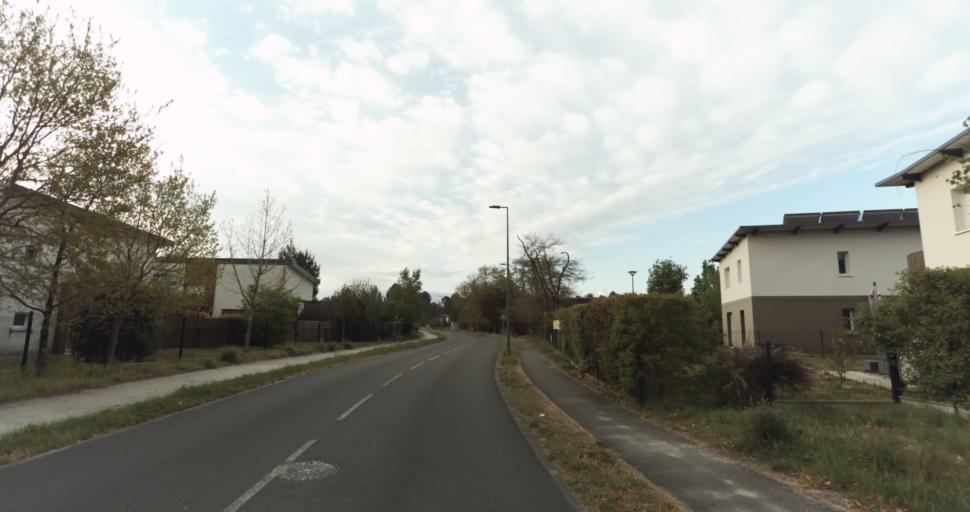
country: FR
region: Aquitaine
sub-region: Departement de la Gironde
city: Martignas-sur-Jalle
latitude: 44.8068
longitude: -0.7721
